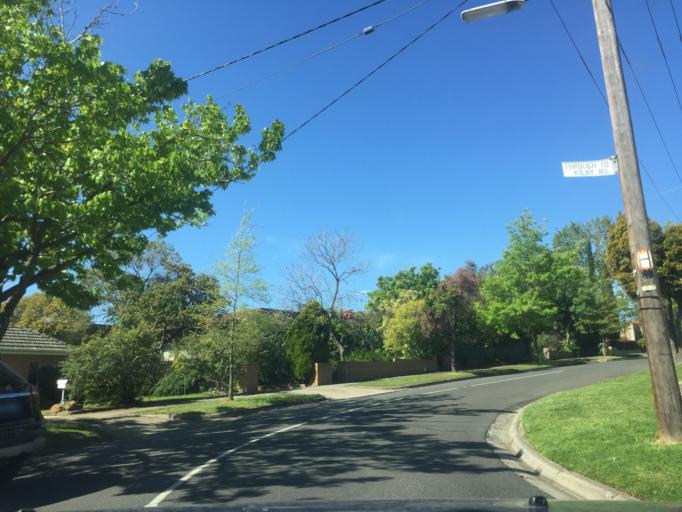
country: AU
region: Victoria
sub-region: Boroondara
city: Kew East
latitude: -37.7922
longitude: 145.0430
